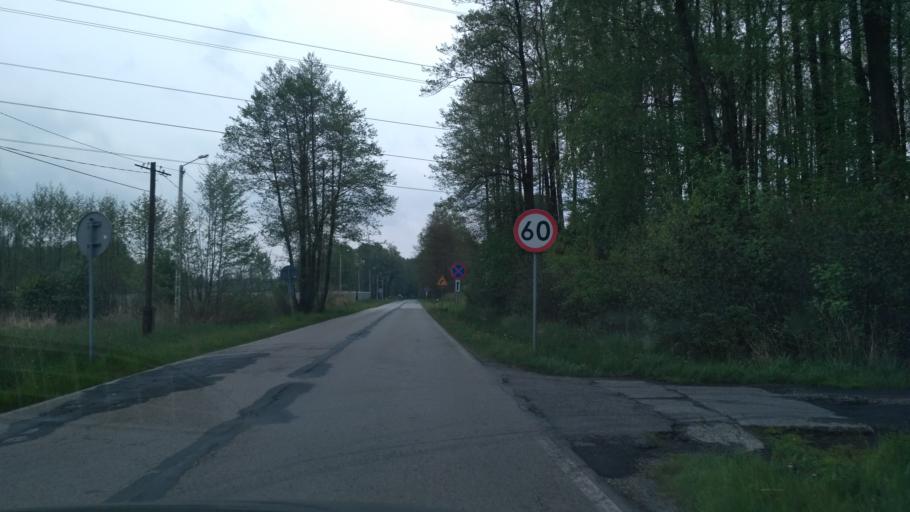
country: PL
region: Subcarpathian Voivodeship
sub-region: Powiat kolbuszowski
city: Kolbuszowa
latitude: 50.1846
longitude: 21.7612
